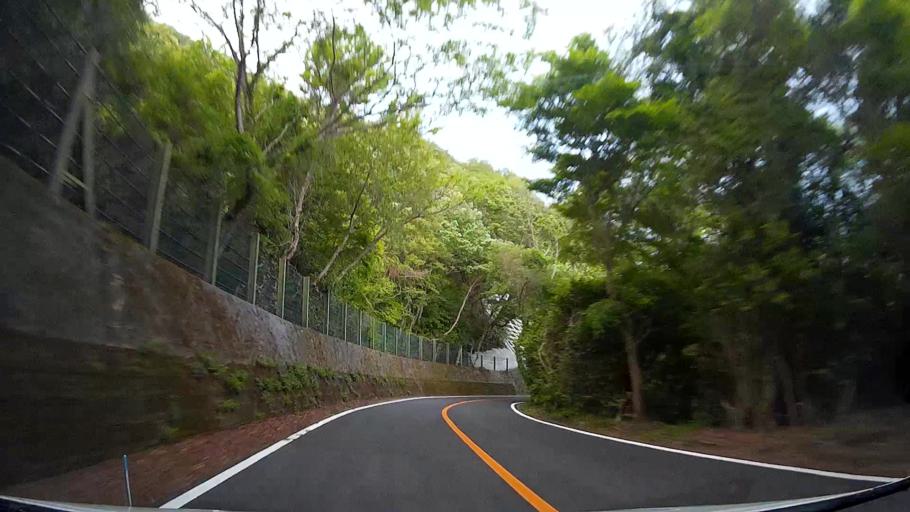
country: JP
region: Kanagawa
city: Yugawara
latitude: 35.1603
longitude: 139.0720
